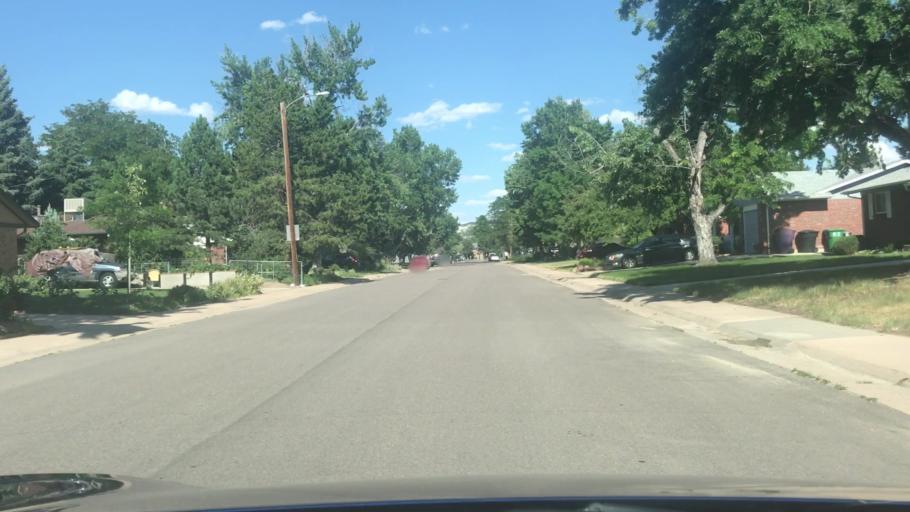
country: US
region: Colorado
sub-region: Arapahoe County
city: Glendale
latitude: 39.6926
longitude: -104.9074
